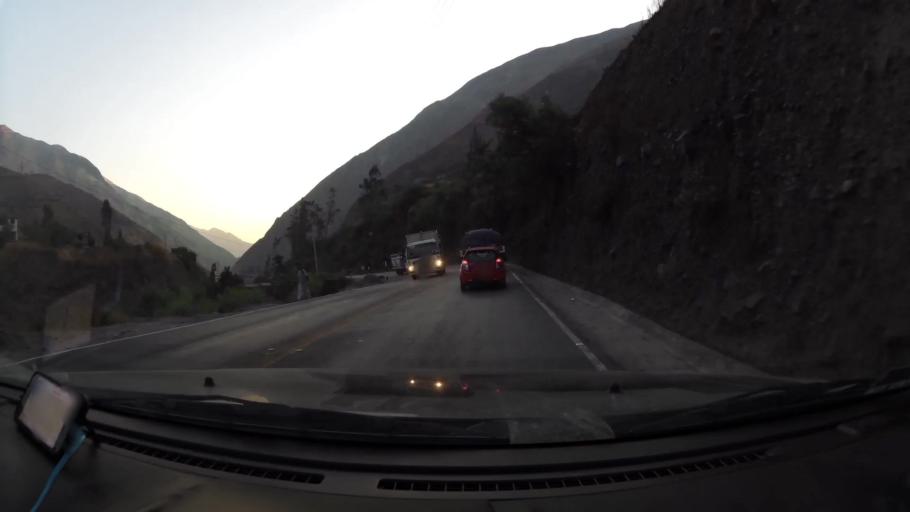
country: PE
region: Lima
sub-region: Provincia de Huarochiri
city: Matucana
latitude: -11.8392
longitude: -76.3778
